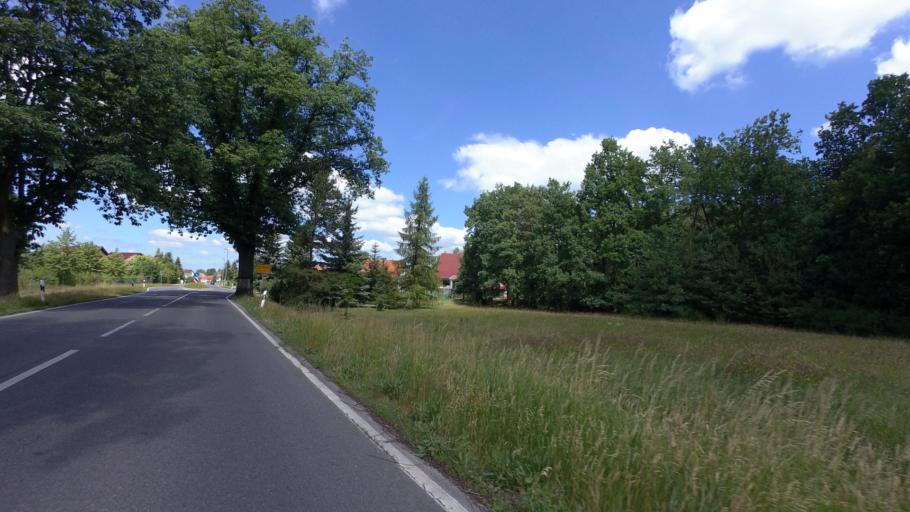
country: DE
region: Brandenburg
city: Sonnewalde
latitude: 51.6630
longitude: 13.6493
